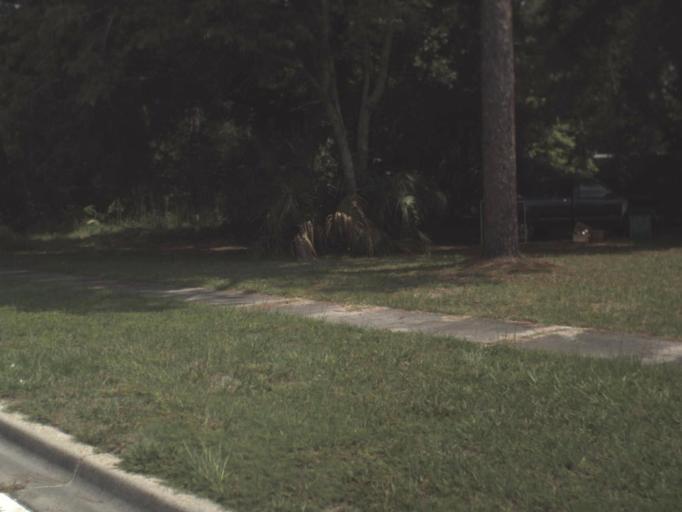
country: US
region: Florida
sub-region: Levy County
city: Chiefland
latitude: 29.4841
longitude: -82.8565
